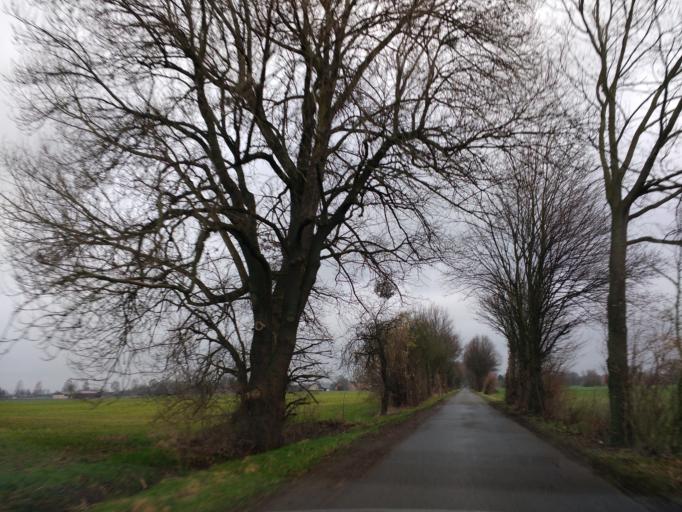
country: DE
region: North Rhine-Westphalia
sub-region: Regierungsbezirk Detmold
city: Salzkotten
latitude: 51.7290
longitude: 8.6335
